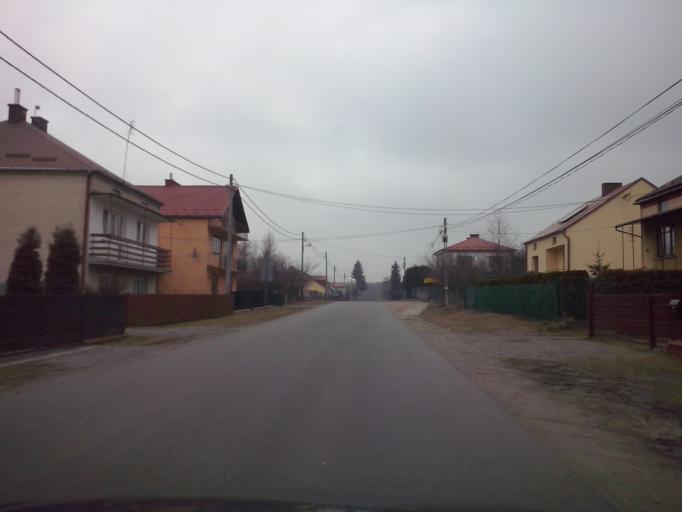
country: PL
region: Subcarpathian Voivodeship
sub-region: Powiat nizanski
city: Bieliny
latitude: 50.4244
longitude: 22.3200
